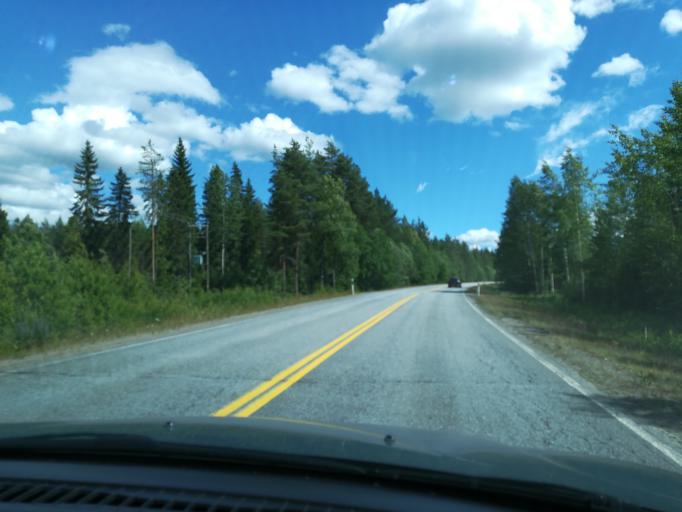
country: FI
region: Southern Savonia
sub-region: Mikkeli
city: Hirvensalmi
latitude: 61.6624
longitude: 26.9624
